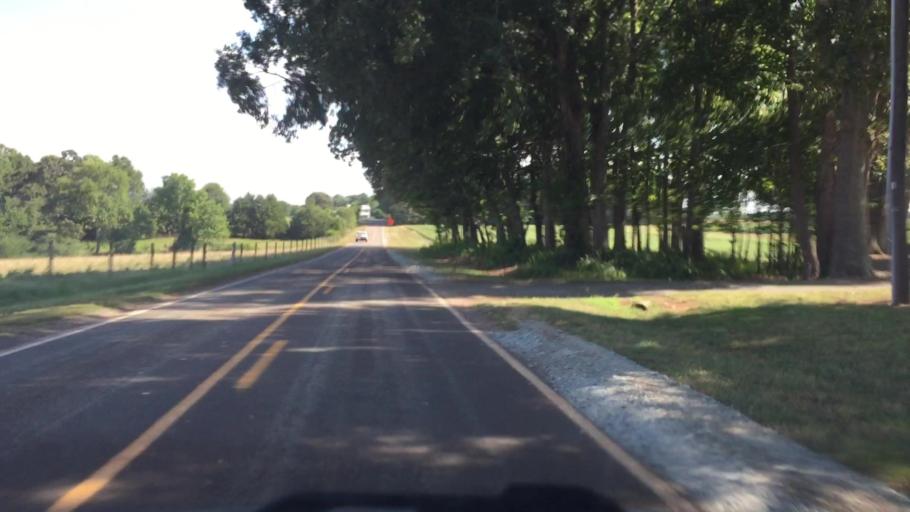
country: US
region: North Carolina
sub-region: Rowan County
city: Enochville
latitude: 35.6399
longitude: -80.6686
